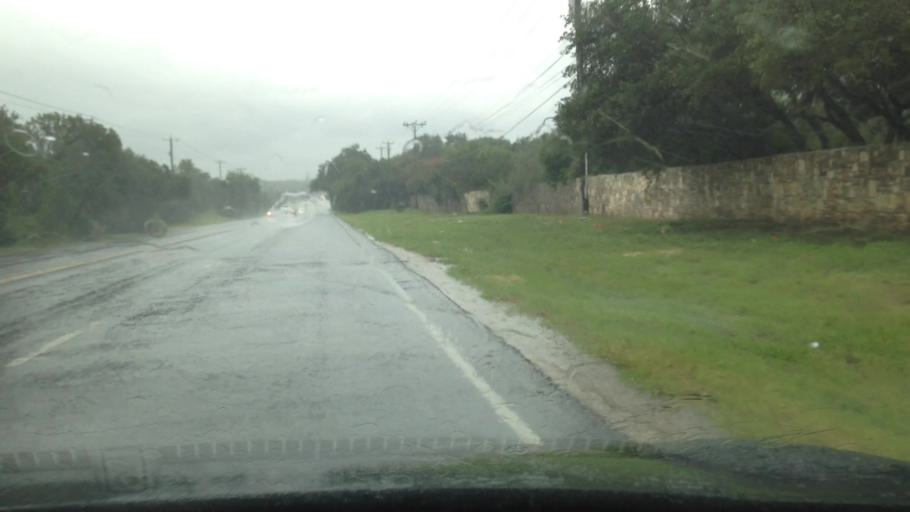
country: US
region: Texas
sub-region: Bexar County
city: Shavano Park
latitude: 29.5803
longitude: -98.5494
